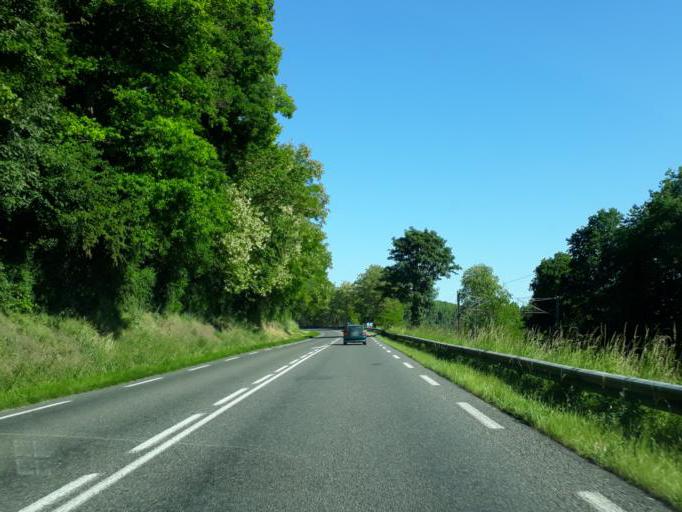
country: FR
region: Bourgogne
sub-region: Departement de la Nievre
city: Neuvy-sur-Loire
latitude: 47.4943
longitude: 2.9142
